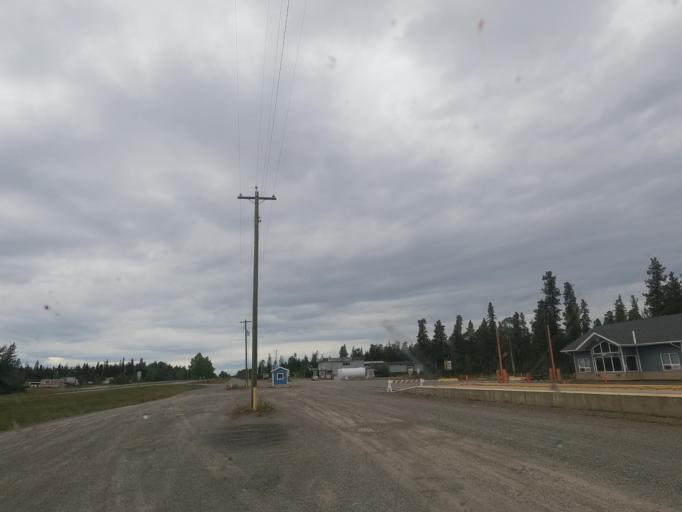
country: CA
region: Yukon
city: Watson Lake
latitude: 60.0492
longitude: -128.6524
